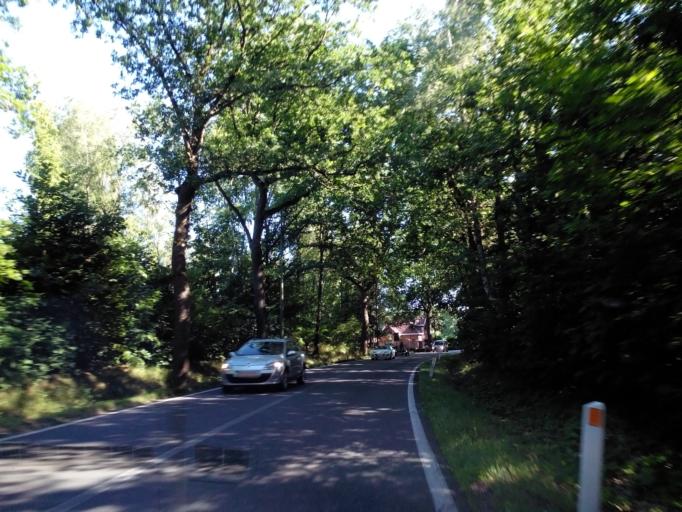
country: BE
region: Flanders
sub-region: Provincie Limburg
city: Opglabbeek
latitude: 51.0605
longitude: 5.5861
